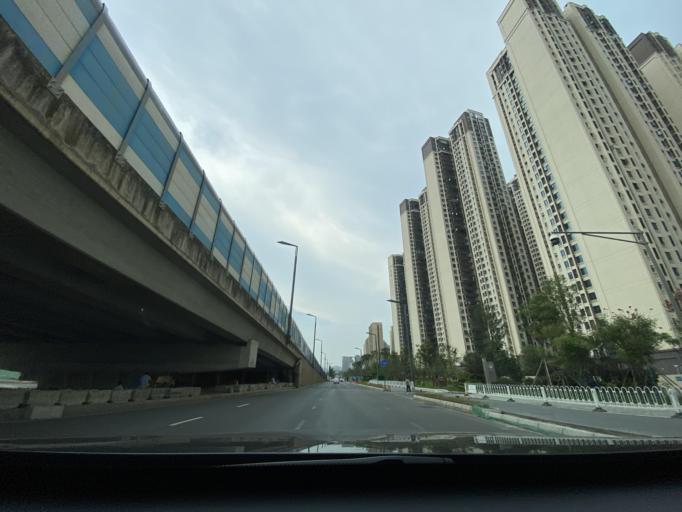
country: CN
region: Sichuan
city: Dongsheng
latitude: 30.4749
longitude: 104.0260
